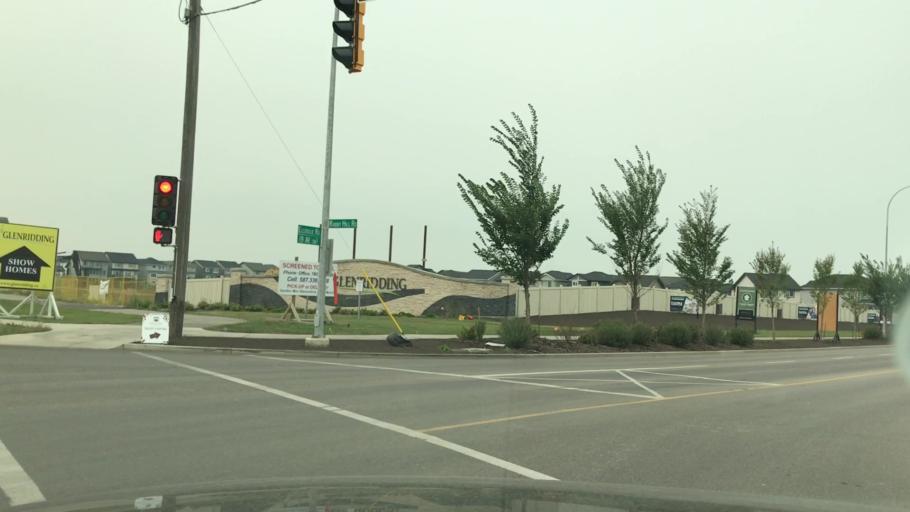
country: CA
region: Alberta
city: Devon
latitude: 53.4249
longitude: -113.5897
